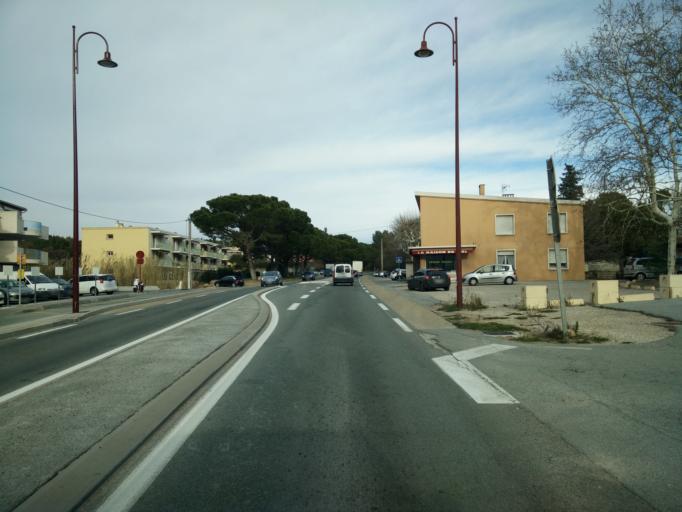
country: FR
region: Provence-Alpes-Cote d'Azur
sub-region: Departement du Var
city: Vidauban
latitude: 43.4319
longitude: 6.4374
